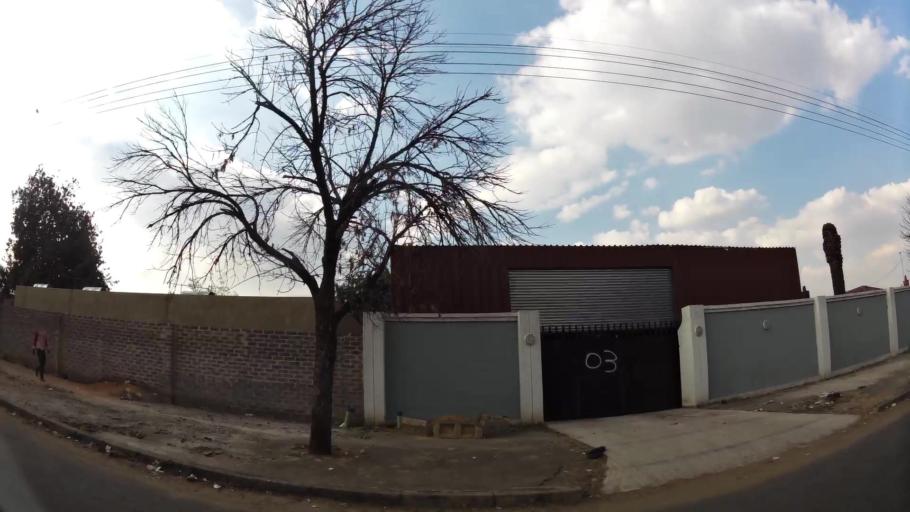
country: ZA
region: Gauteng
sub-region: Ekurhuleni Metropolitan Municipality
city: Germiston
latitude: -26.2269
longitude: 28.1801
